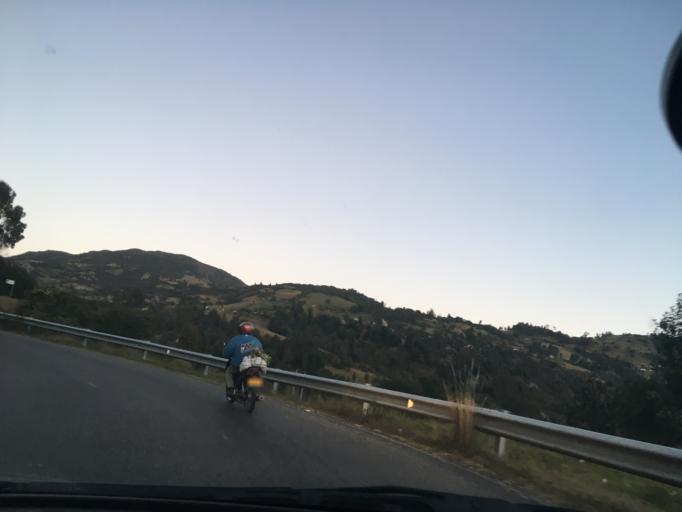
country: CO
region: Boyaca
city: Aquitania
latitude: 5.6145
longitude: -72.9091
